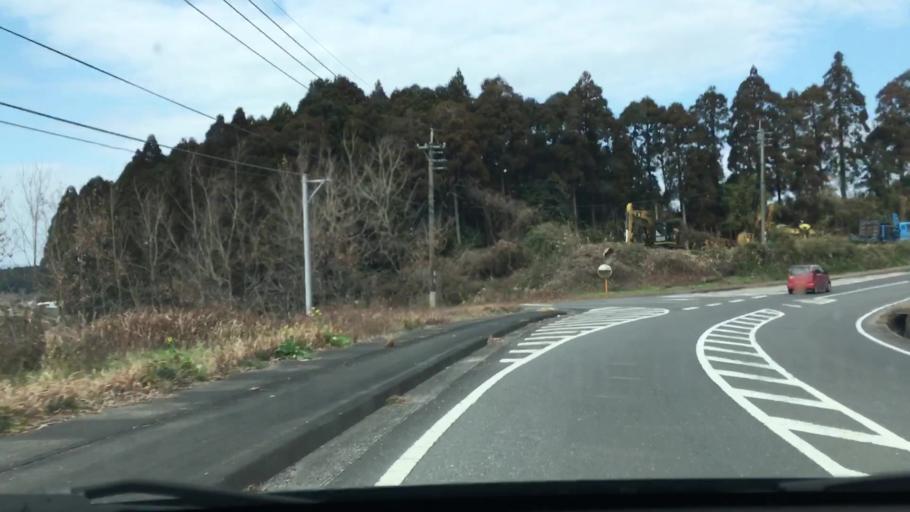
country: JP
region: Miyazaki
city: Kushima
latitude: 31.5039
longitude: 131.2391
